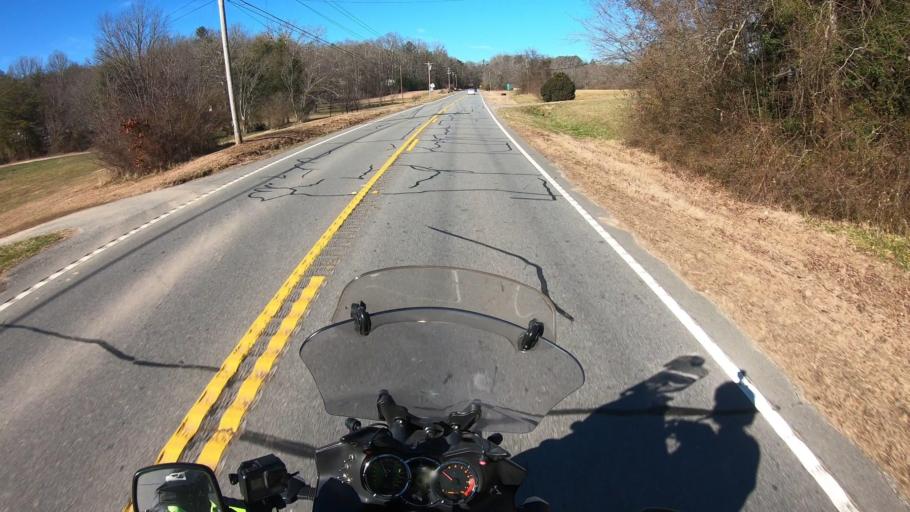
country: US
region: Georgia
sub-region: Fannin County
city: McCaysville
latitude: 34.9451
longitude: -84.3175
